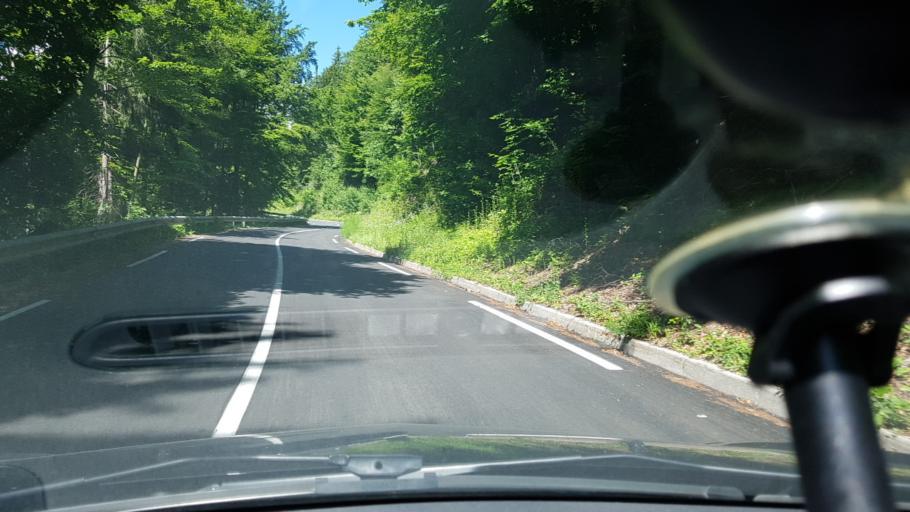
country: SI
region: Zrece
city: Zrece
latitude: 46.4069
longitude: 15.3668
